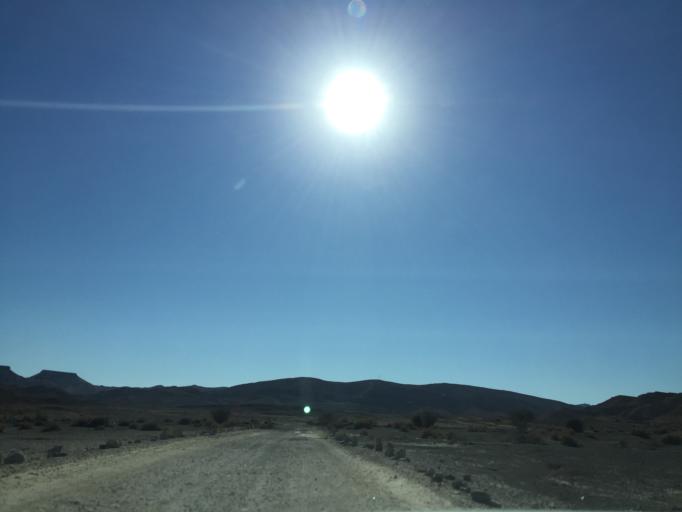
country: IL
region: Southern District
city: Mitzpe Ramon
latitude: 30.6032
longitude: 34.8966
